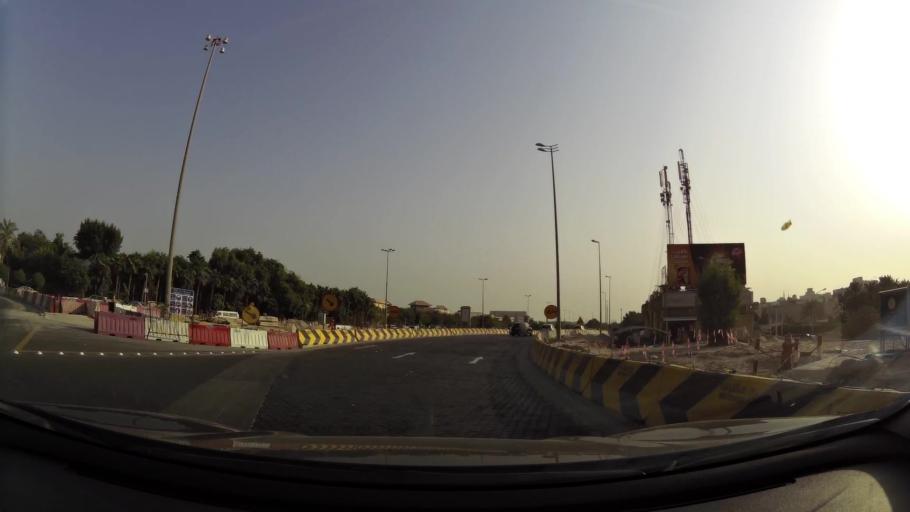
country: KW
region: Muhafazat Hawalli
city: As Salimiyah
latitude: 29.3228
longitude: 48.0879
